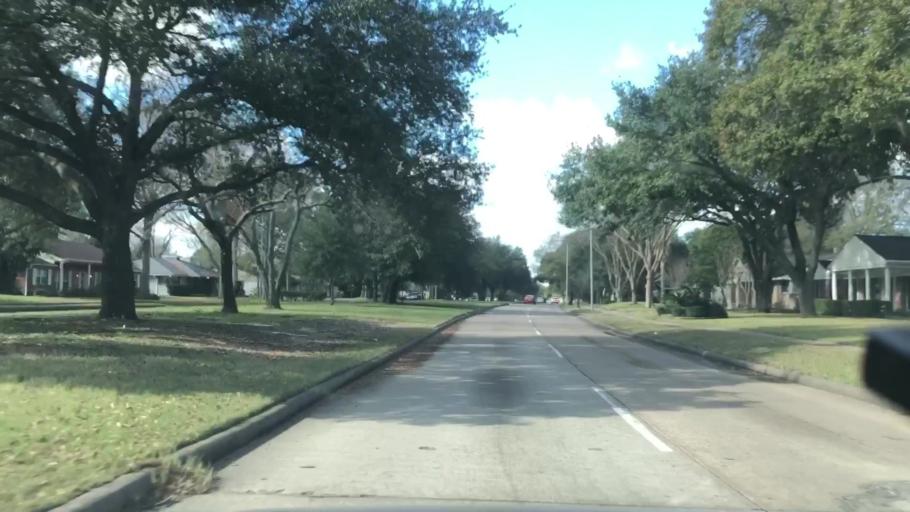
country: US
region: Texas
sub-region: Harris County
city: Bellaire
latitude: 29.6574
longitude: -95.4832
